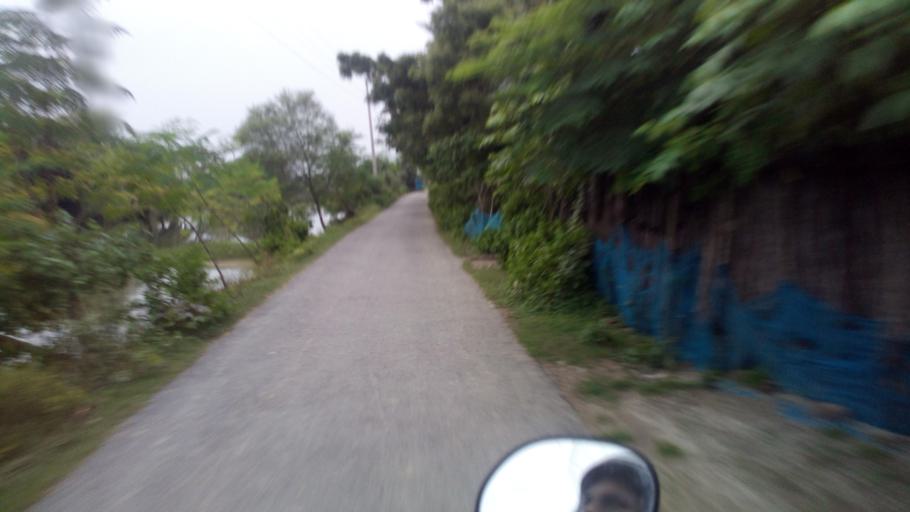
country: BD
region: Khulna
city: Phultala
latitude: 22.7739
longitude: 89.4072
